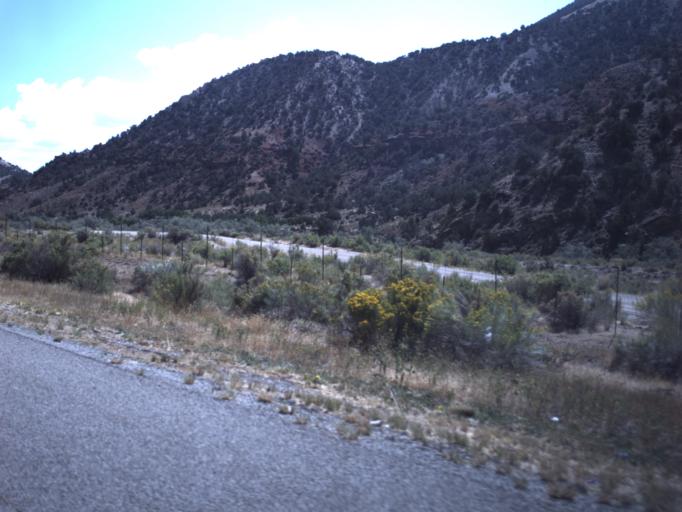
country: US
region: Utah
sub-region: Sevier County
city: Salina
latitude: 38.9329
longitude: -111.7996
